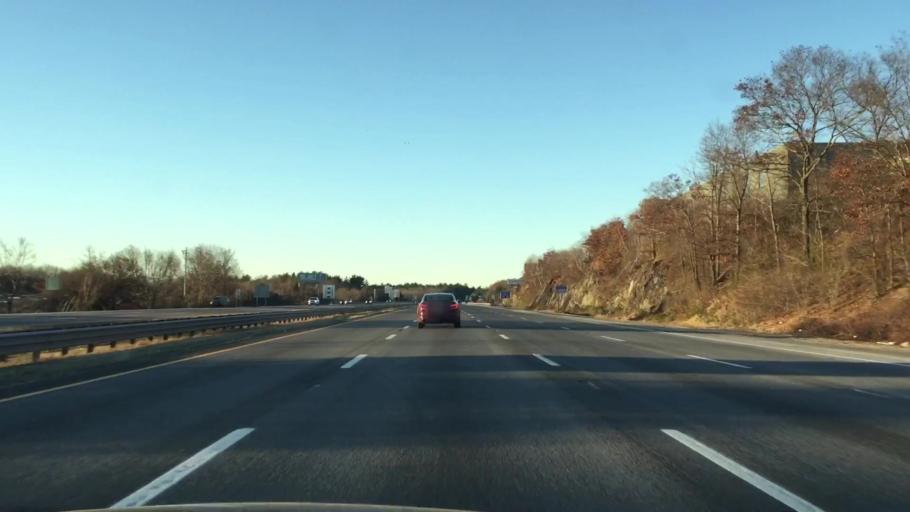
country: US
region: Massachusetts
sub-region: Norfolk County
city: Braintree
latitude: 42.2190
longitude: -71.0374
